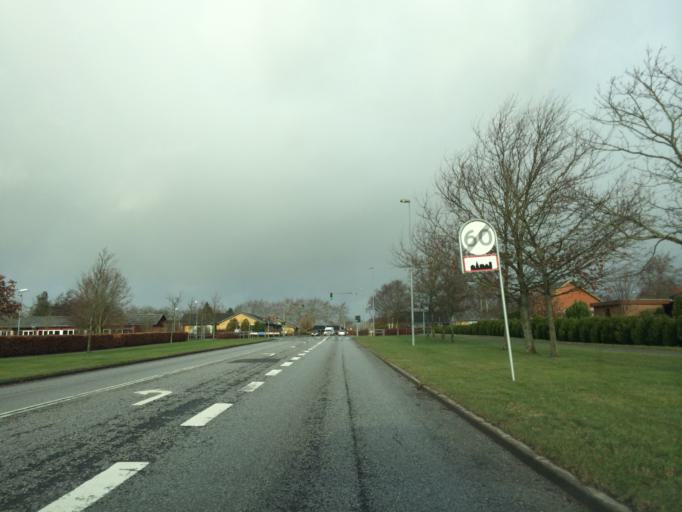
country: DK
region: Central Jutland
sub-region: Herning Kommune
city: Vildbjerg
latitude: 56.1923
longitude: 8.7613
